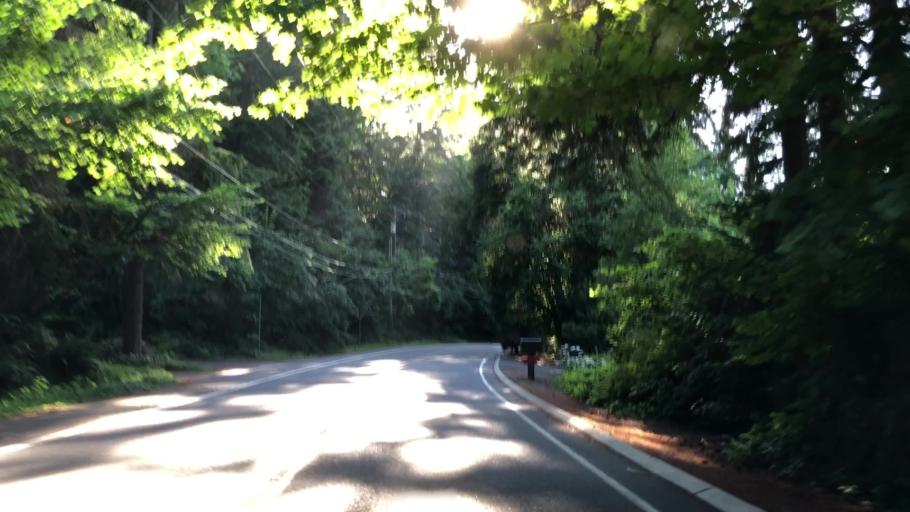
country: US
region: Washington
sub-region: King County
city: Woodinville
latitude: 47.7580
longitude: -122.1232
